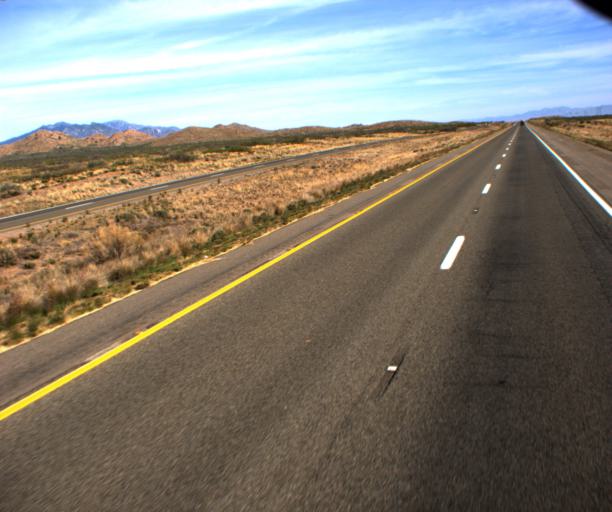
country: US
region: Arizona
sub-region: Graham County
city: Swift Trail Junction
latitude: 32.4900
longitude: -109.6733
